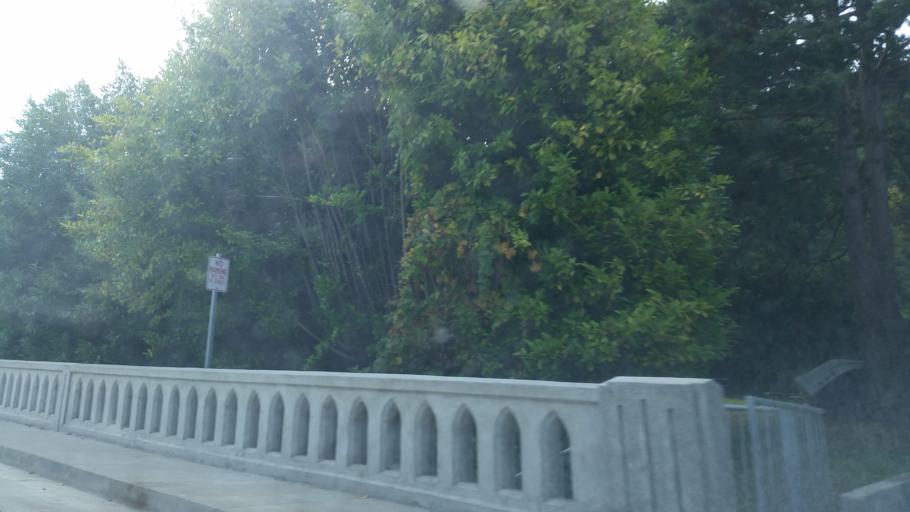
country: US
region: Oregon
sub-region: Clatsop County
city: Astoria
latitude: 46.1853
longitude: -123.8222
